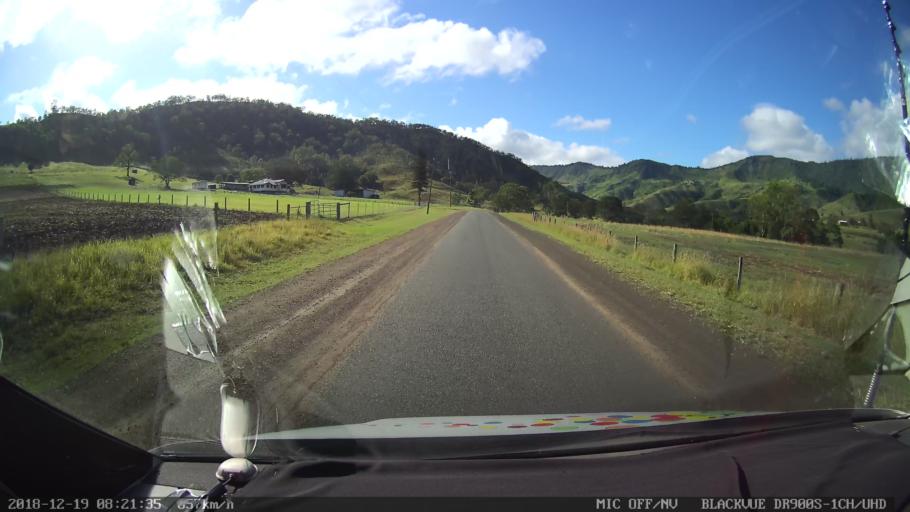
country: AU
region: New South Wales
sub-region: Kyogle
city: Kyogle
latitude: -28.2982
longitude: 152.9103
